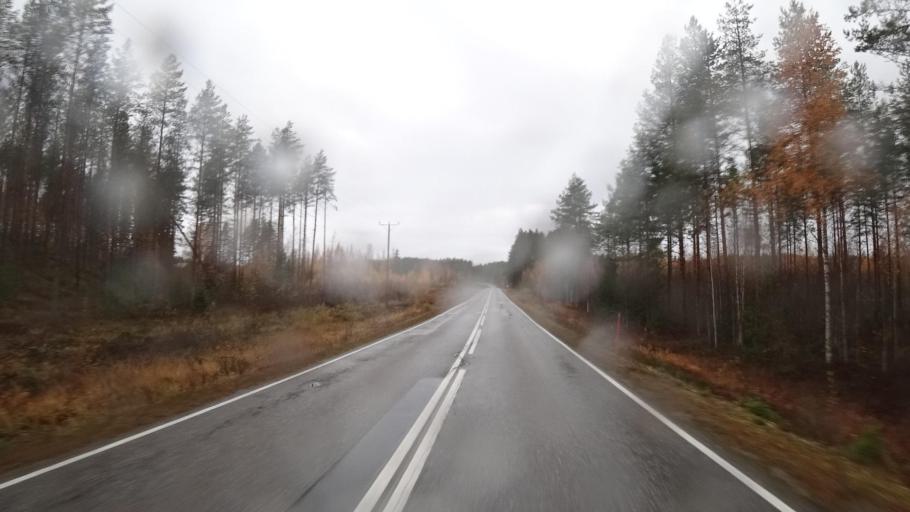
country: FI
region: North Karelia
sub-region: Joensuu
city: Outokumpu
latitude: 62.6197
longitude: 28.9338
